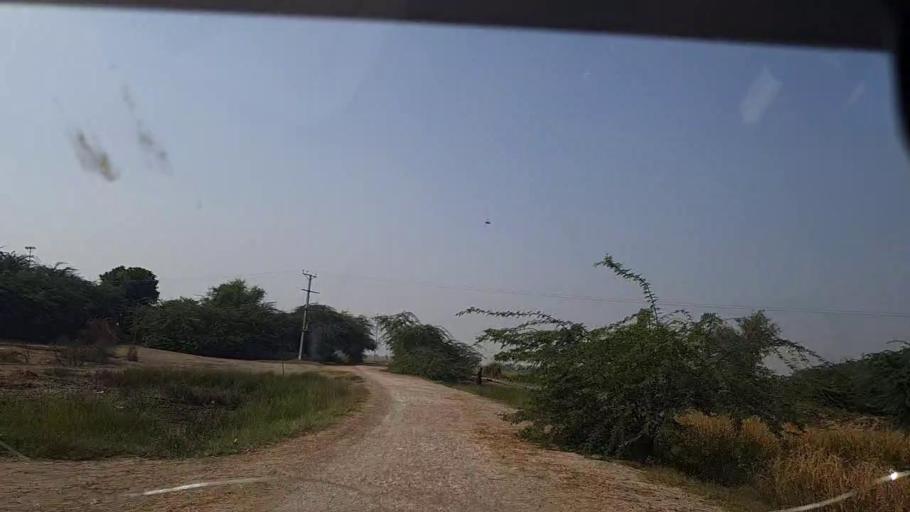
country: PK
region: Sindh
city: Shikarpur
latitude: 28.0909
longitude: 68.6047
